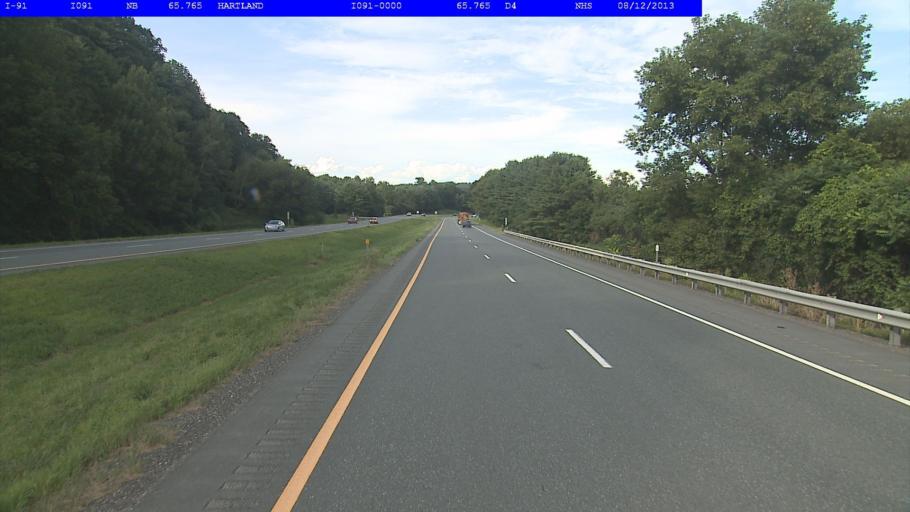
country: US
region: Vermont
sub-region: Windsor County
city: White River Junction
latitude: 43.5897
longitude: -72.3597
